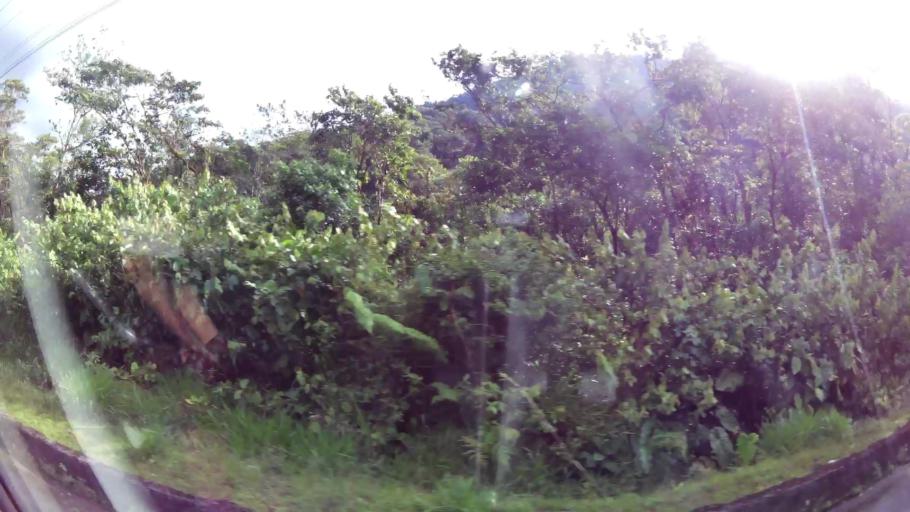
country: EC
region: Pastaza
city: Puyo
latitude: -1.4152
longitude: -78.1810
